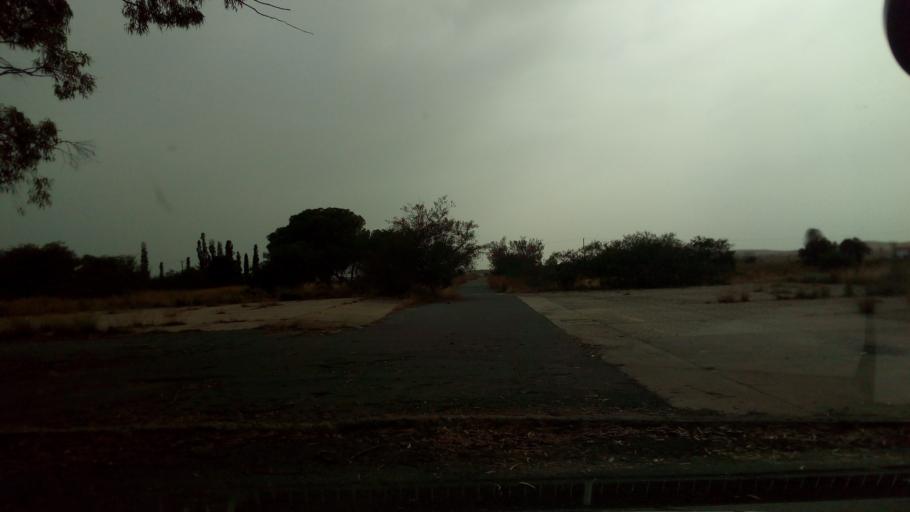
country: CY
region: Larnaka
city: Pyla
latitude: 35.0197
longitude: 33.7028
